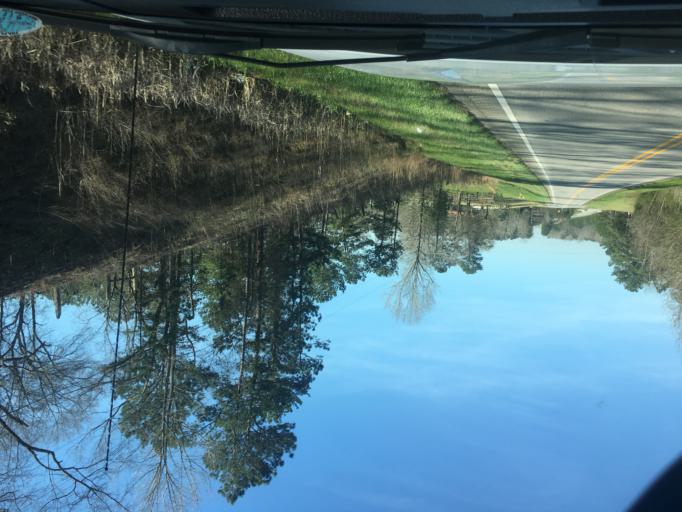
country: US
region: Alabama
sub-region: Lee County
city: Auburn
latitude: 32.4343
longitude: -85.4735
